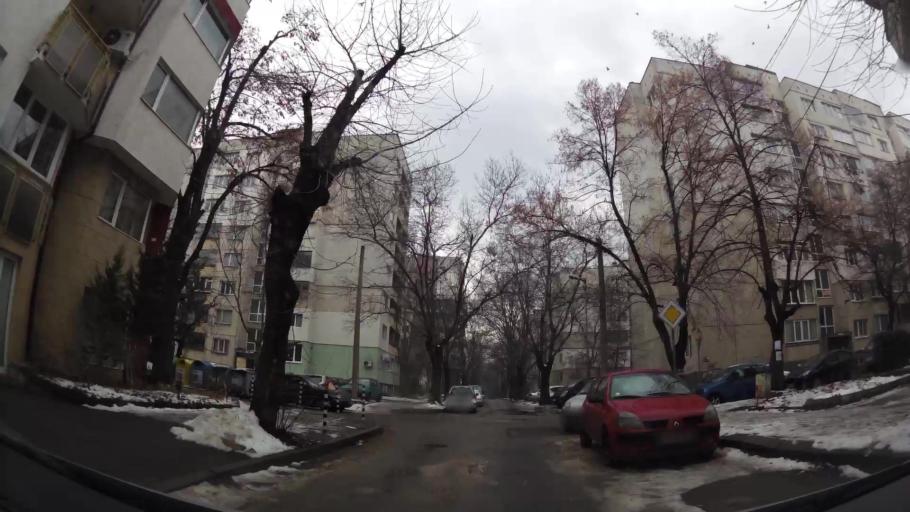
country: BG
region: Sofia-Capital
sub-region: Stolichna Obshtina
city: Sofia
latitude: 42.6884
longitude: 23.2962
